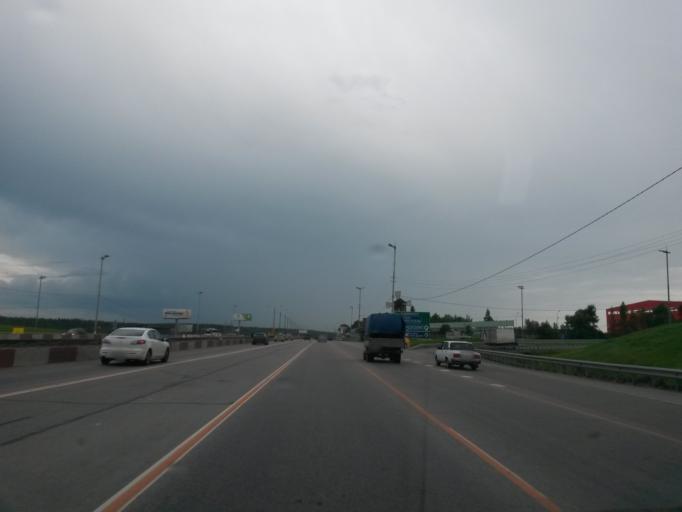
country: RU
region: Moskovskaya
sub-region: Podol'skiy Rayon
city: Podol'sk
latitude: 55.4363
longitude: 37.6151
